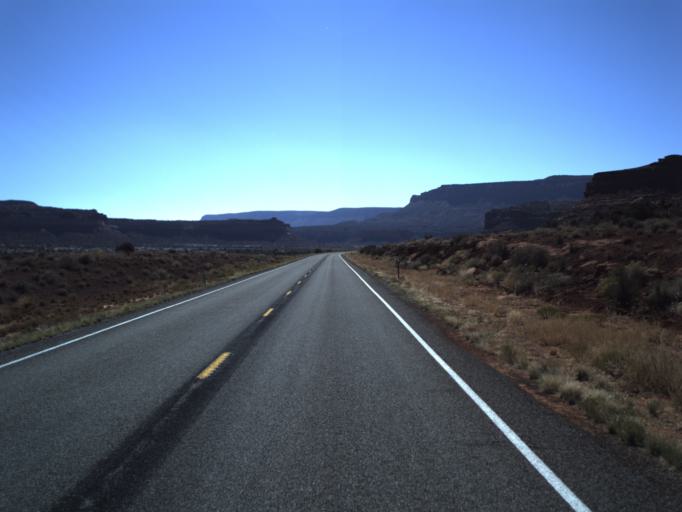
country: US
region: Utah
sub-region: San Juan County
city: Blanding
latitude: 37.7793
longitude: -110.2912
